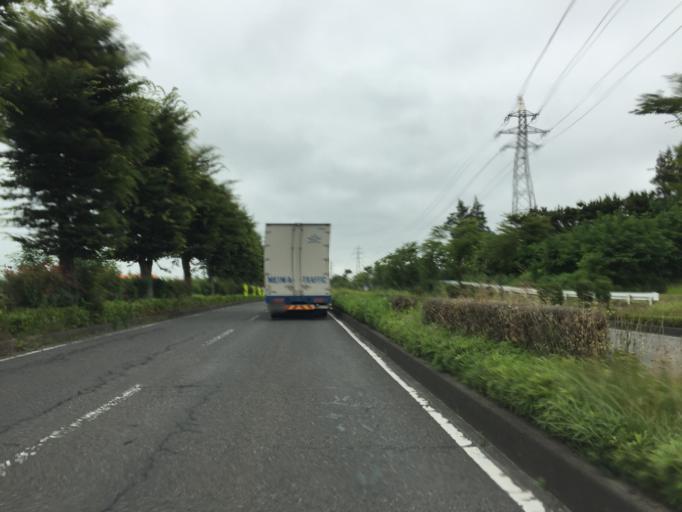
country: JP
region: Fukushima
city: Sukagawa
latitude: 37.2706
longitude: 140.3728
